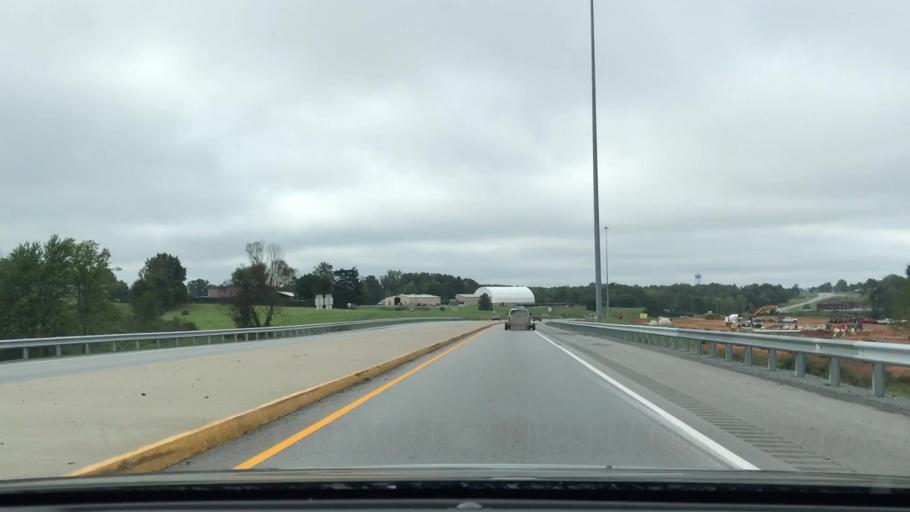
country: US
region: Kentucky
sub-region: Russell County
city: Russell Springs
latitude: 37.0499
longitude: -85.0701
